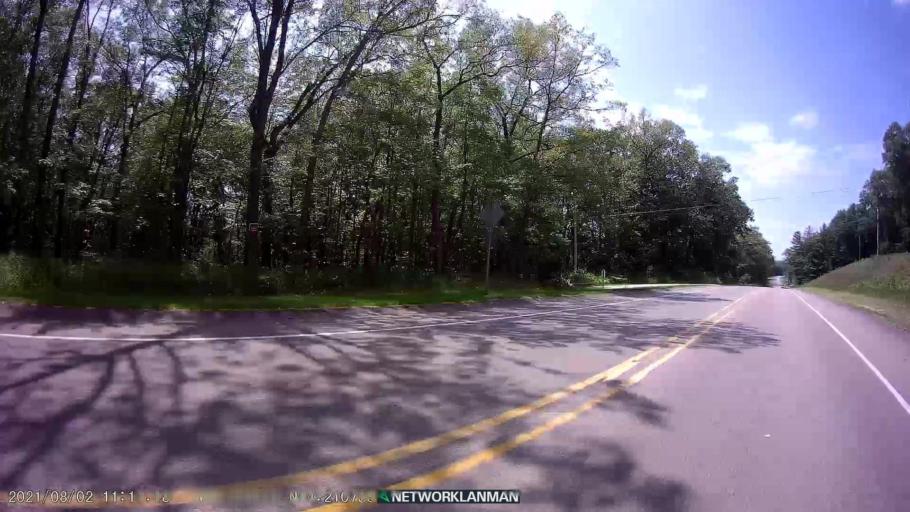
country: US
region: Michigan
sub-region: Manistee County
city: Manistee
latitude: 44.2108
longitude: -86.2550
